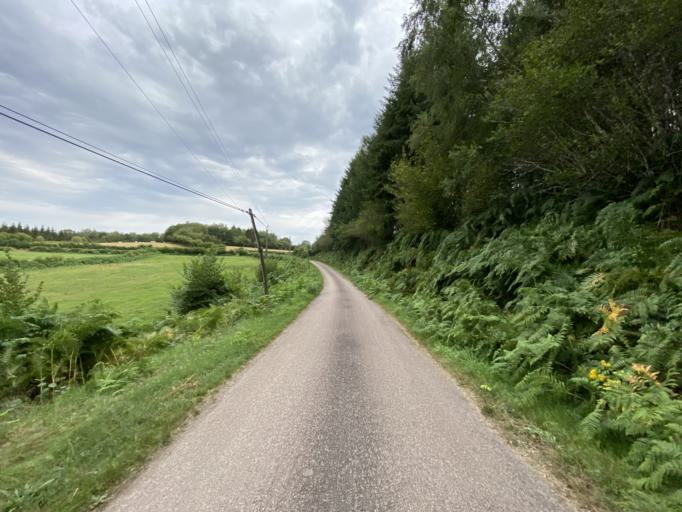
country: FR
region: Bourgogne
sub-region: Departement de la Cote-d'Or
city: Saulieu
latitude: 47.2623
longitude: 4.1363
